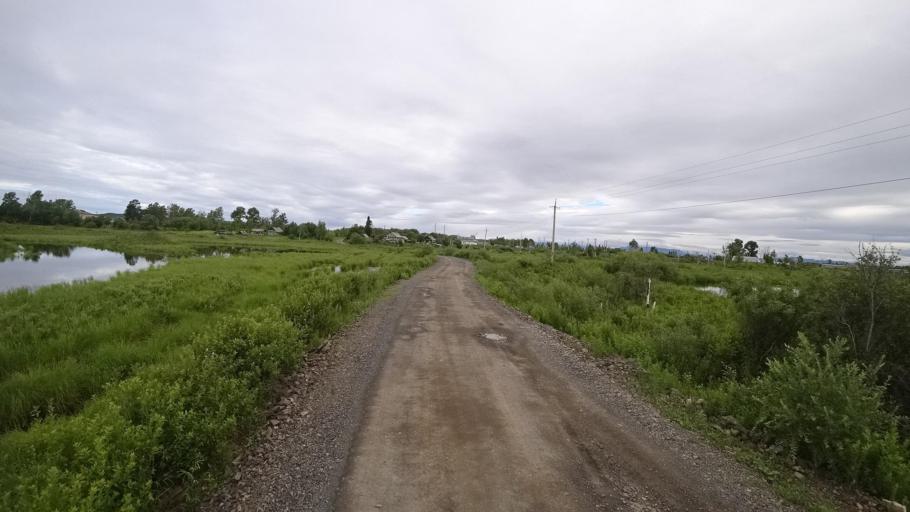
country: RU
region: Khabarovsk Krai
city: Amursk
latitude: 49.9019
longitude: 136.1469
